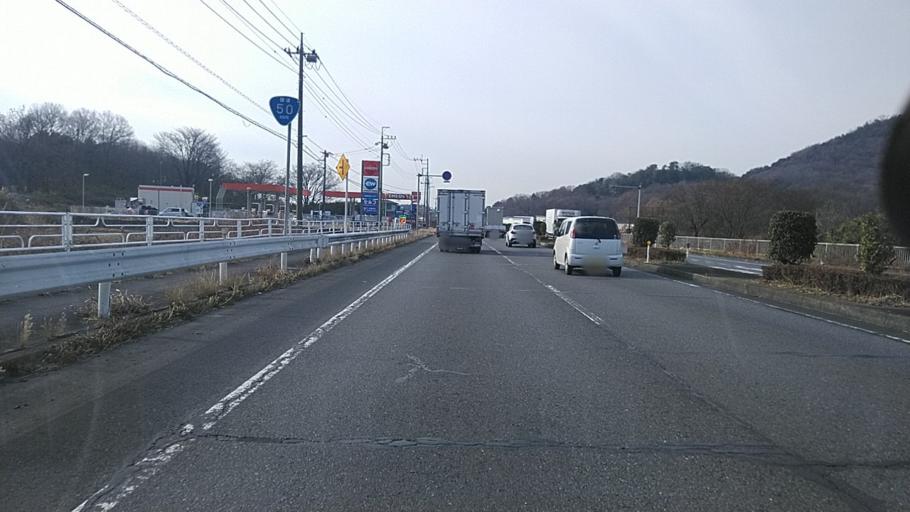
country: JP
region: Tochigi
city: Sano
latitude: 36.3054
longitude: 139.6379
